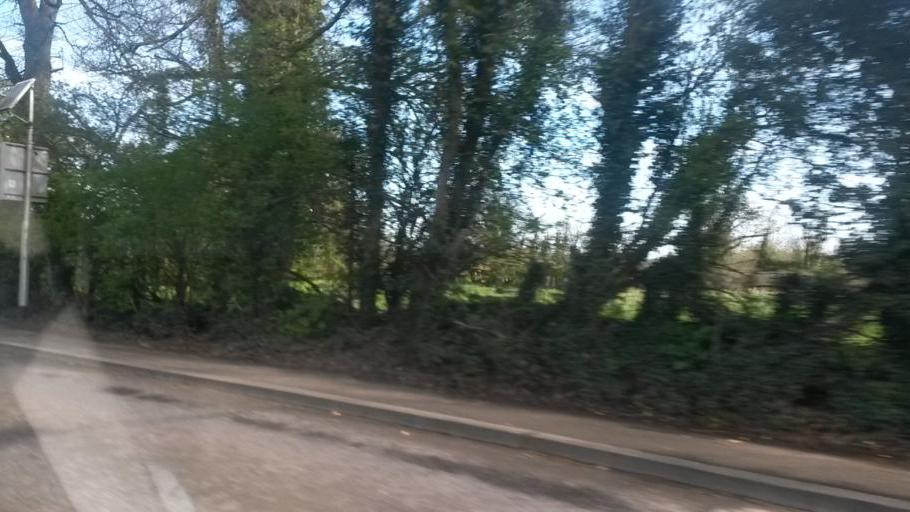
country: IE
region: Leinster
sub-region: An Mhi
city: Kells
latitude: 53.7255
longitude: -6.8680
